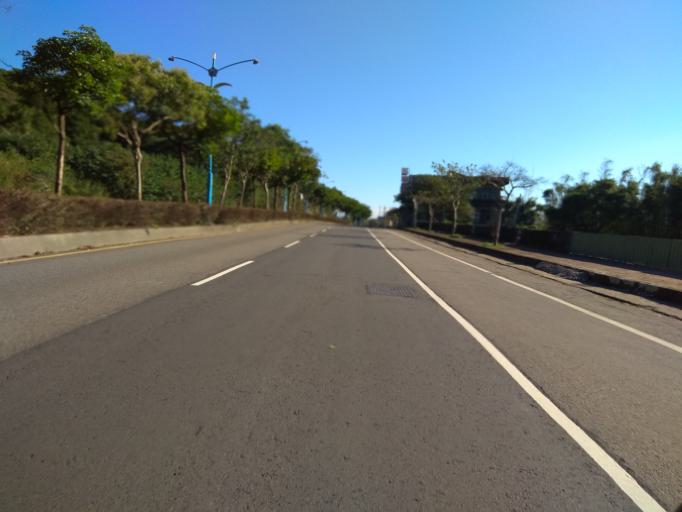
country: TW
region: Taiwan
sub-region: Hsinchu
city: Zhubei
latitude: 24.8965
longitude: 121.1126
